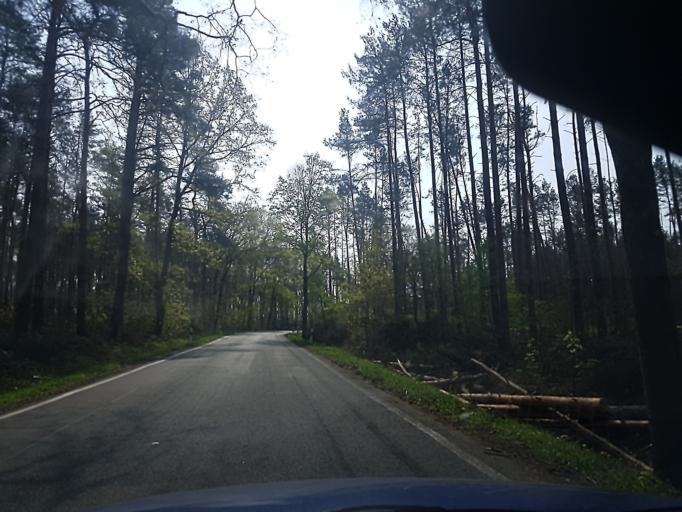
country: DE
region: Saxony
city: Arzberg
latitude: 51.5873
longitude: 13.1465
